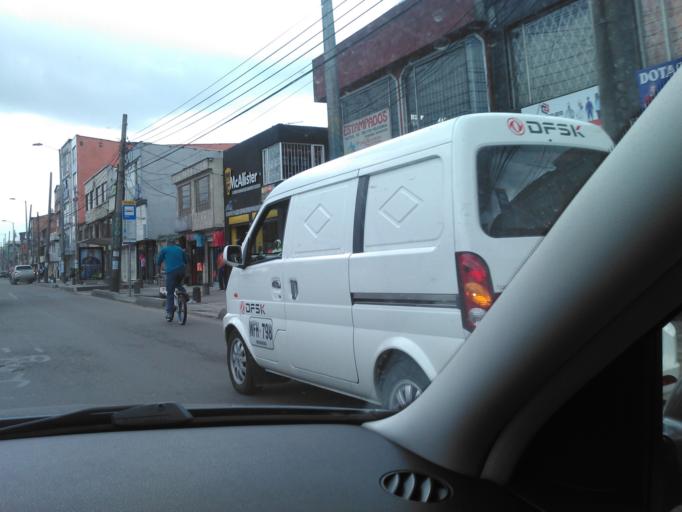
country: CO
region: Bogota D.C.
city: Bogota
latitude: 4.6140
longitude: -74.1274
